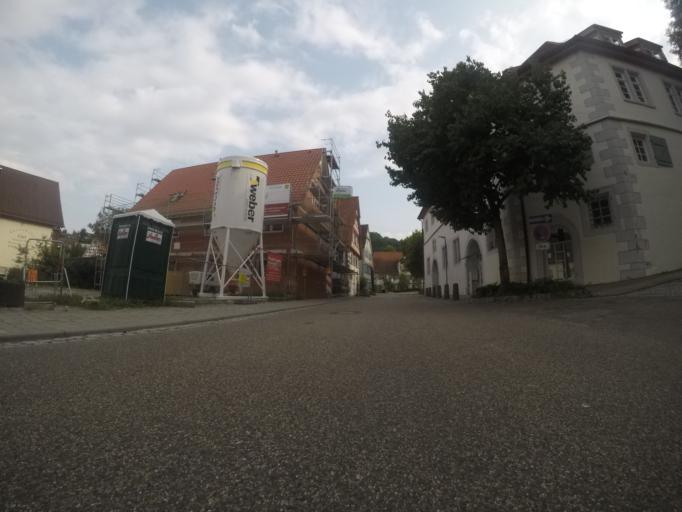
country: DE
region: Baden-Wuerttemberg
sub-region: Regierungsbezirk Stuttgart
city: Eberdingen
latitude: 48.8790
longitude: 8.9650
